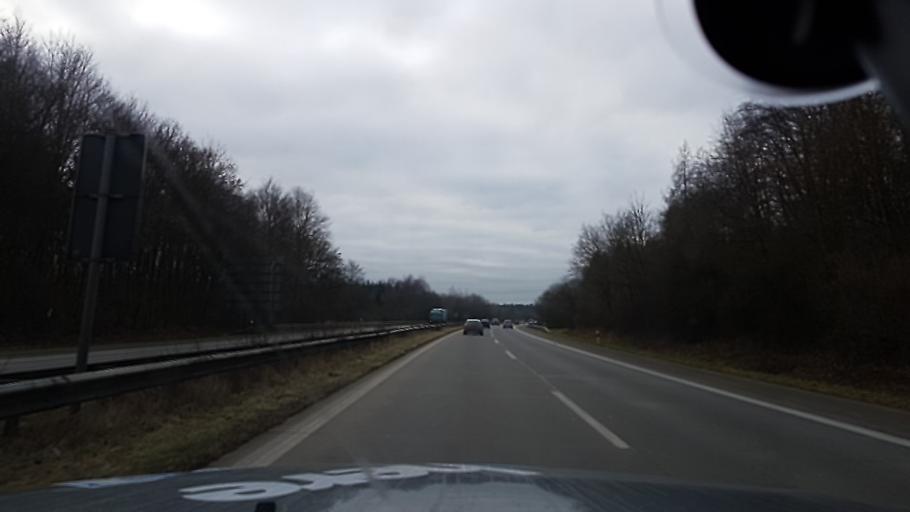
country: DE
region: Schleswig-Holstein
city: Ratekau
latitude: 53.9418
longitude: 10.7449
